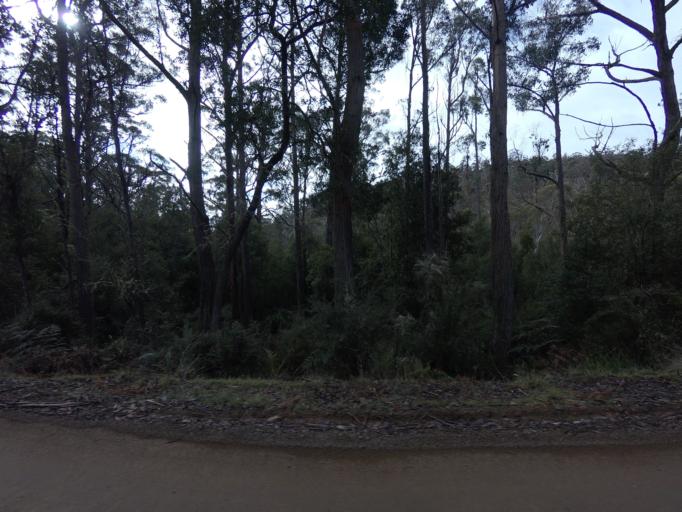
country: AU
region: Tasmania
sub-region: Derwent Valley
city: New Norfolk
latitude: -42.7452
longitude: 146.8662
